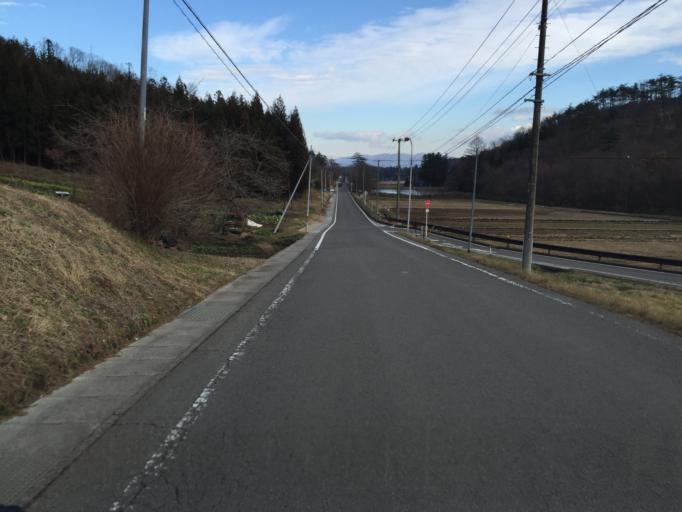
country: JP
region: Fukushima
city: Fukushima-shi
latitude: 37.6770
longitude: 140.4375
